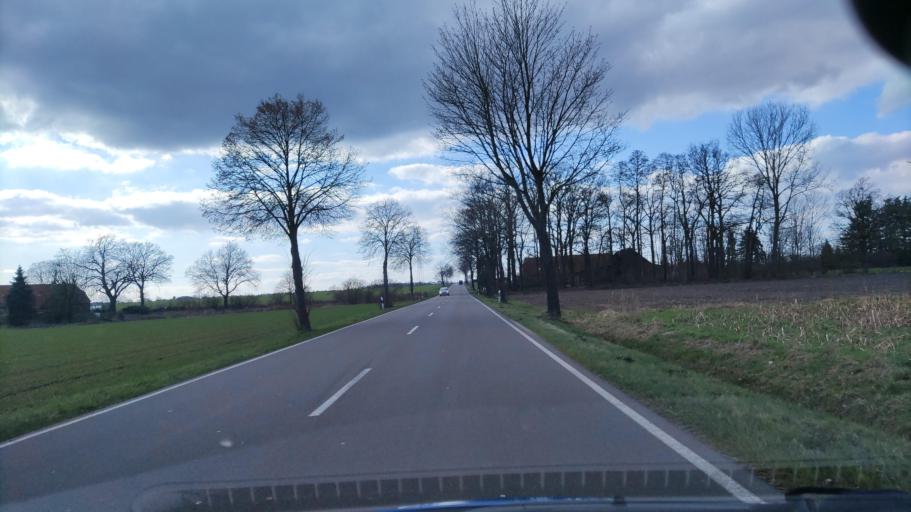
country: DE
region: Lower Saxony
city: Beedenbostel
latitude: 52.6406
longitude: 10.2503
